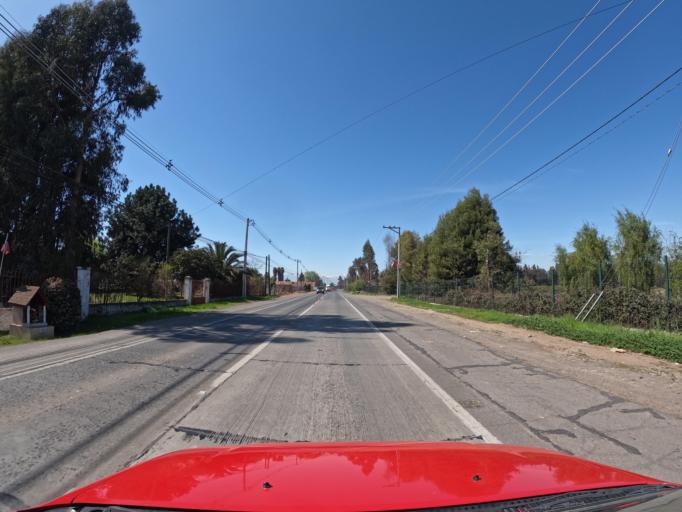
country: CL
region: Maule
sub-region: Provincia de Curico
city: Curico
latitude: -34.9639
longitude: -71.1822
